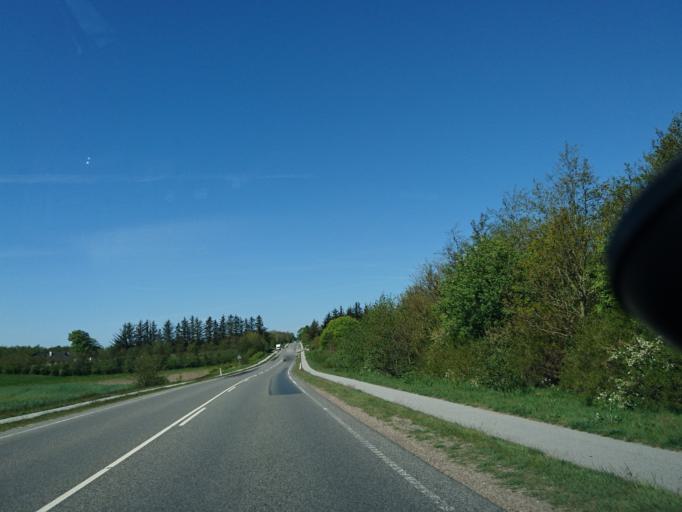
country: DK
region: North Denmark
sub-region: Hjorring Kommune
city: Tars
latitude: 57.4552
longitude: 10.1124
